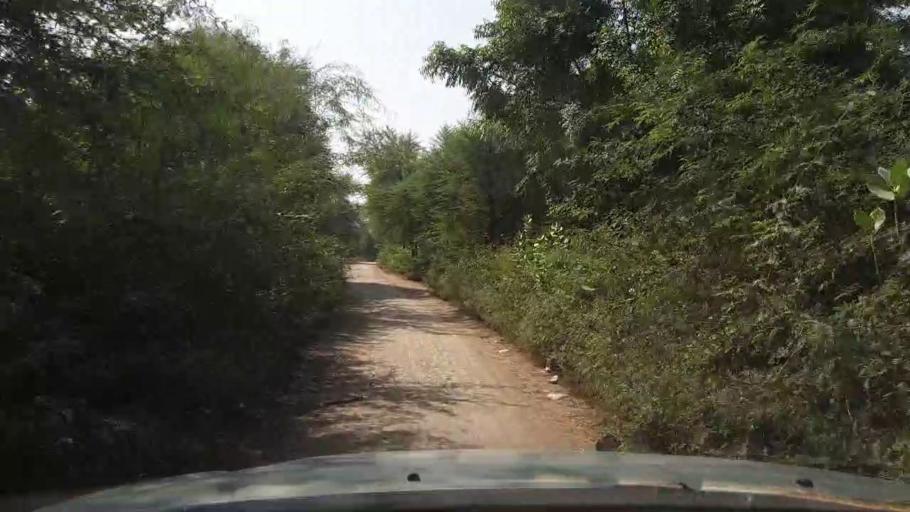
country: PK
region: Sindh
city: Tando Jam
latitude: 25.3689
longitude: 68.5307
